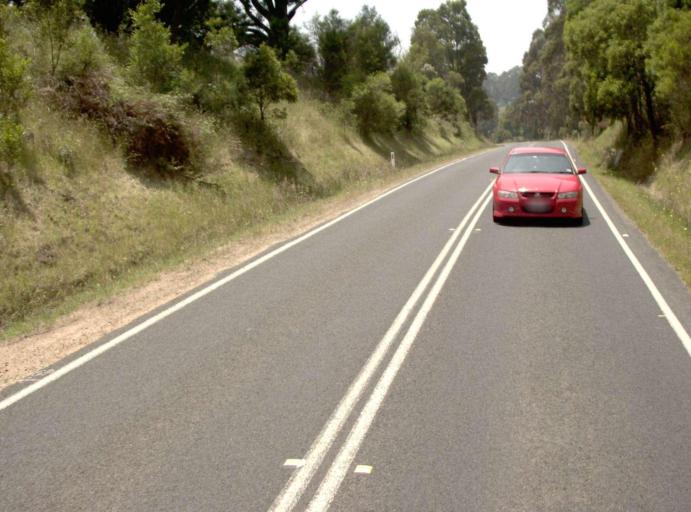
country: AU
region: Victoria
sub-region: Latrobe
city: Traralgon
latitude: -38.3441
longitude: 146.7224
